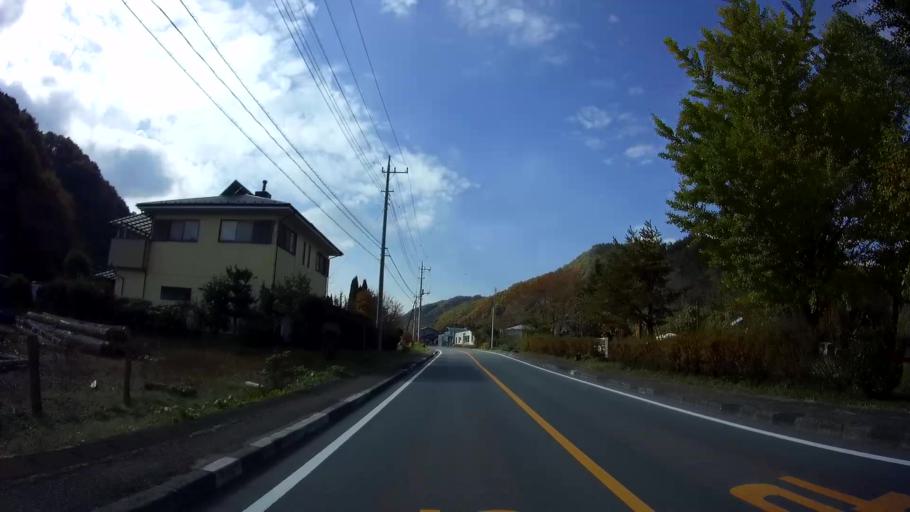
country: JP
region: Gunma
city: Nakanojomachi
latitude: 36.5127
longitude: 138.7626
